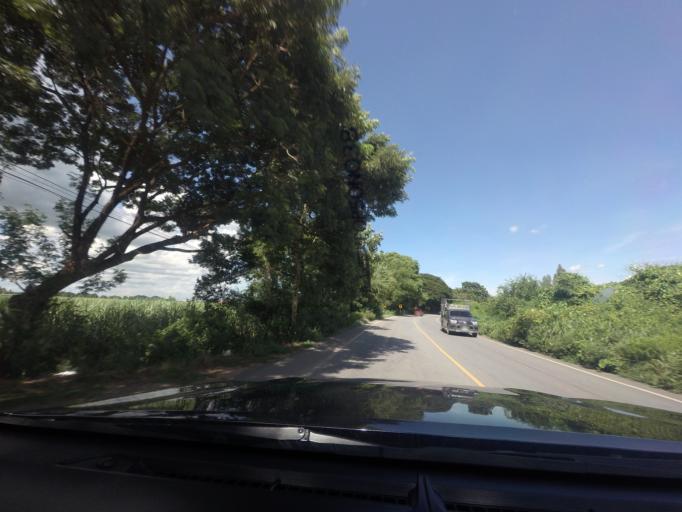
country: TH
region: Kanchanaburi
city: Phanom Thuan
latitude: 14.1778
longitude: 99.7880
